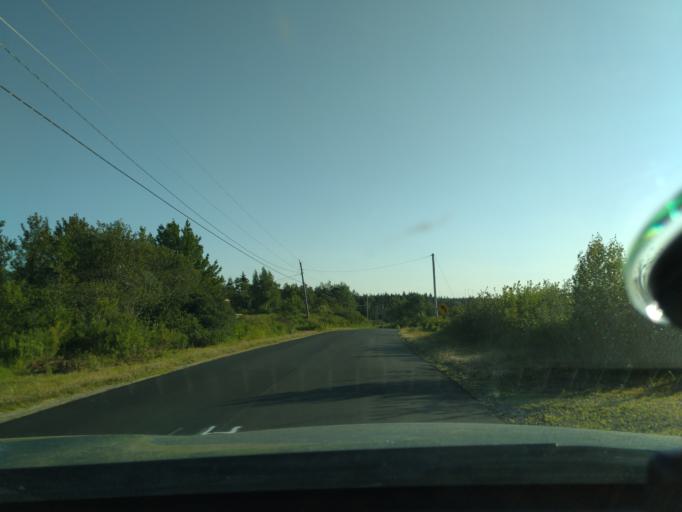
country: US
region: Maine
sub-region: Washington County
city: Machiasport
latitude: 44.6783
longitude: -67.1900
